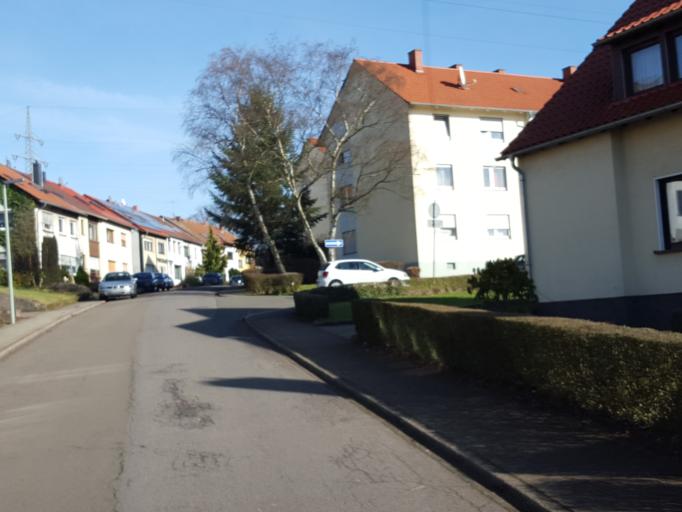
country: DE
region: Saarland
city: Puttlingen
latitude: 49.2846
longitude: 6.8992
